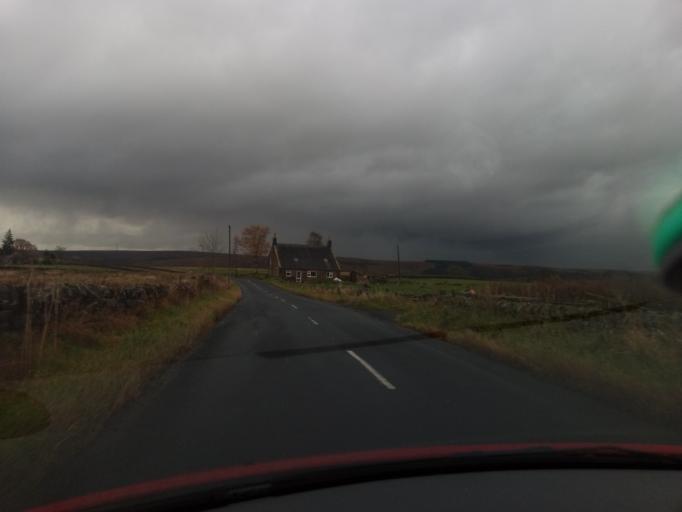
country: GB
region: England
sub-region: Northumberland
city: Corsenside
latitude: 55.1549
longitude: -2.2580
